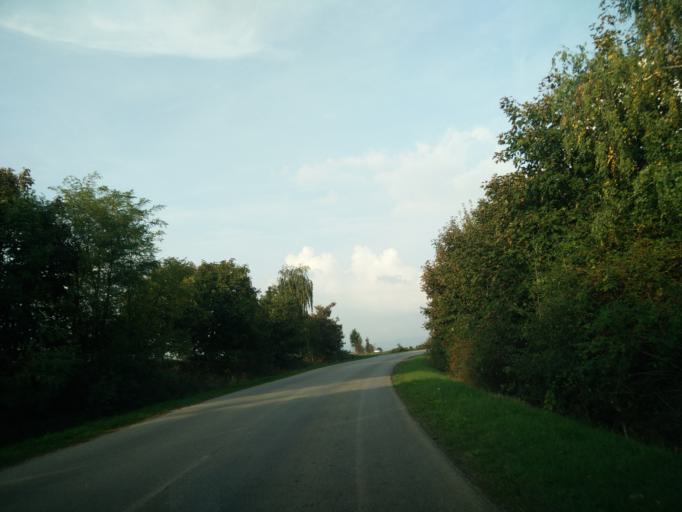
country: SK
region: Nitriansky
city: Banovce nad Bebravou
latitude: 48.7534
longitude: 18.2015
